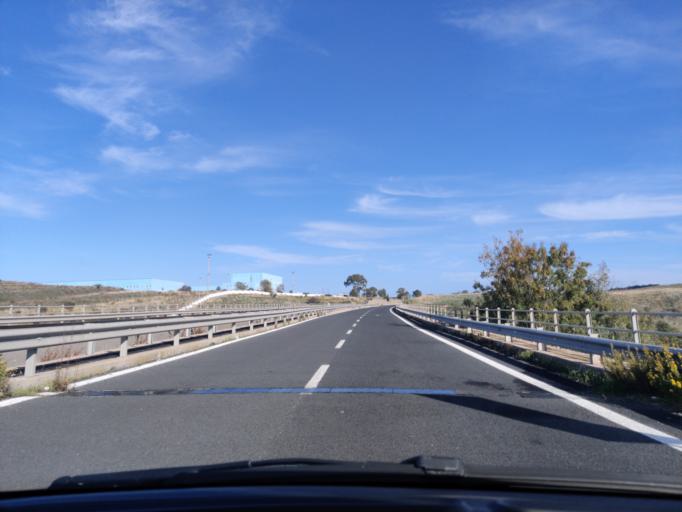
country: IT
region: Latium
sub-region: Citta metropolitana di Roma Capitale
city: Aurelia
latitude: 42.1210
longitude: 11.7911
